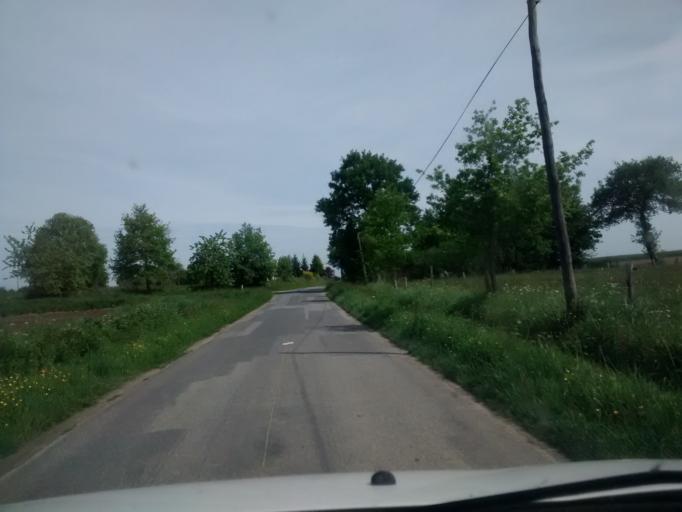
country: FR
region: Brittany
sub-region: Departement d'Ille-et-Vilaine
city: Pleine-Fougeres
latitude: 48.5042
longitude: -1.5251
